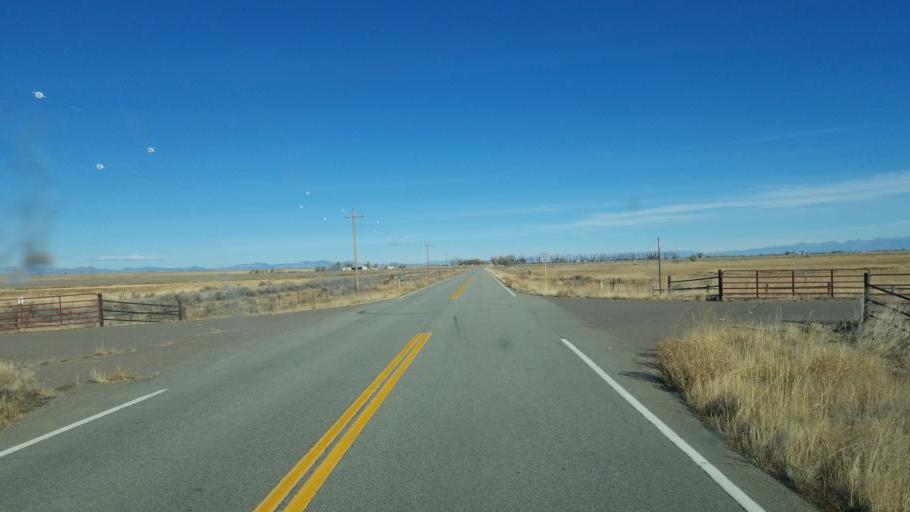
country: US
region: Colorado
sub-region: Rio Grande County
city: Monte Vista
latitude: 37.4685
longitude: -106.1486
